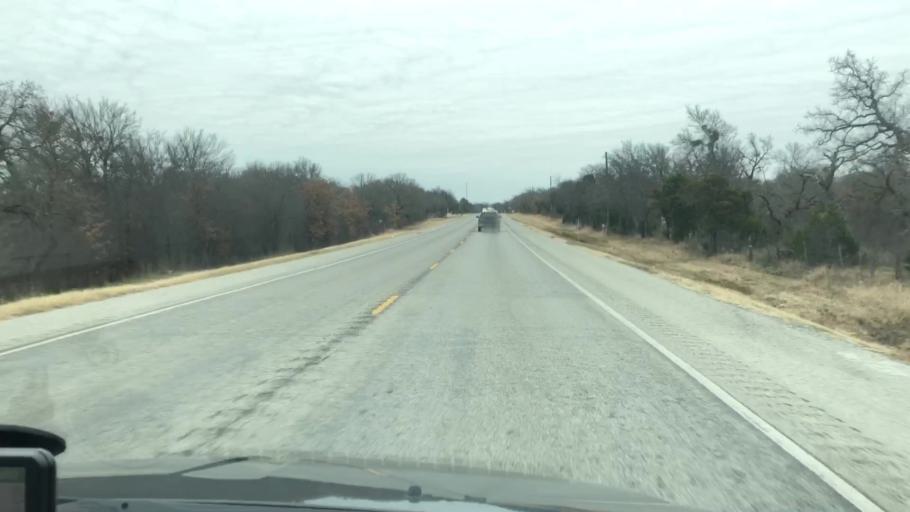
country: US
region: Texas
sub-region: Palo Pinto County
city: Mineral Wells
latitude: 32.8949
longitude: -98.0861
